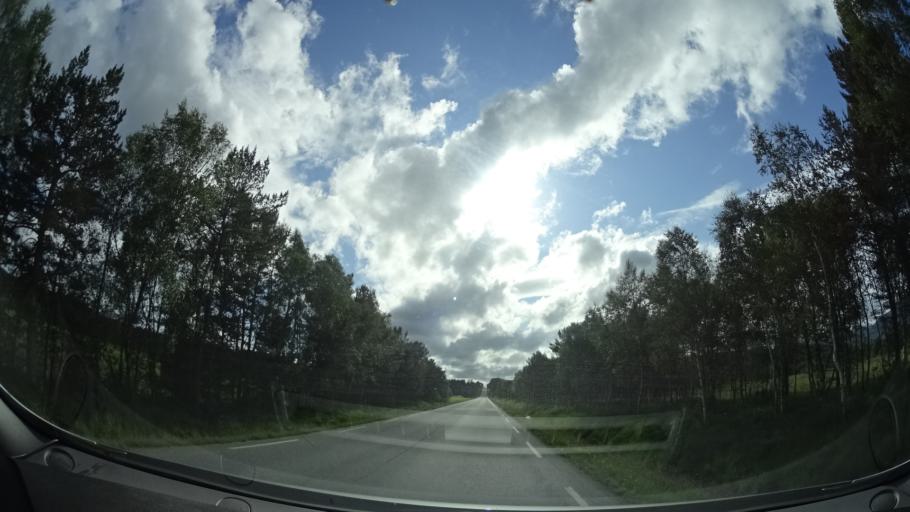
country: NO
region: More og Romsdal
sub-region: Halsa
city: Liaboen
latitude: 63.1268
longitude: 8.3683
